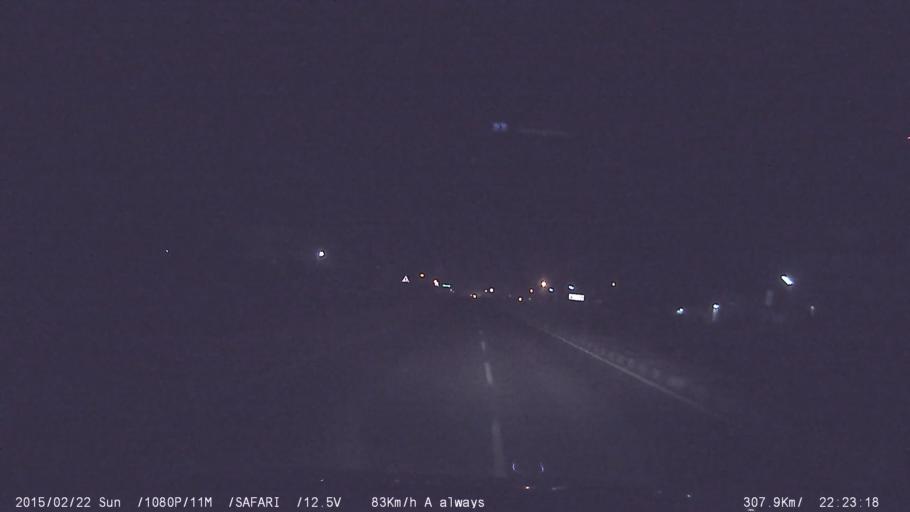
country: IN
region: Tamil Nadu
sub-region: Karur
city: Karur
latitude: 11.0236
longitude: 78.0659
